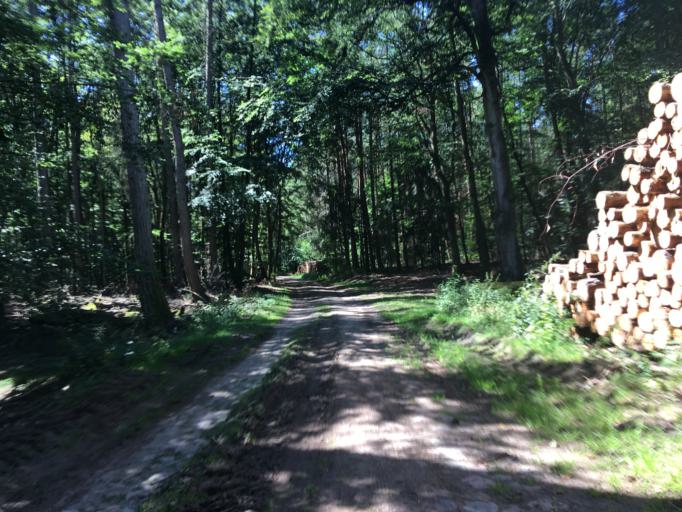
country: DE
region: Brandenburg
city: Grosswoltersdorf
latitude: 53.1329
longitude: 13.0183
